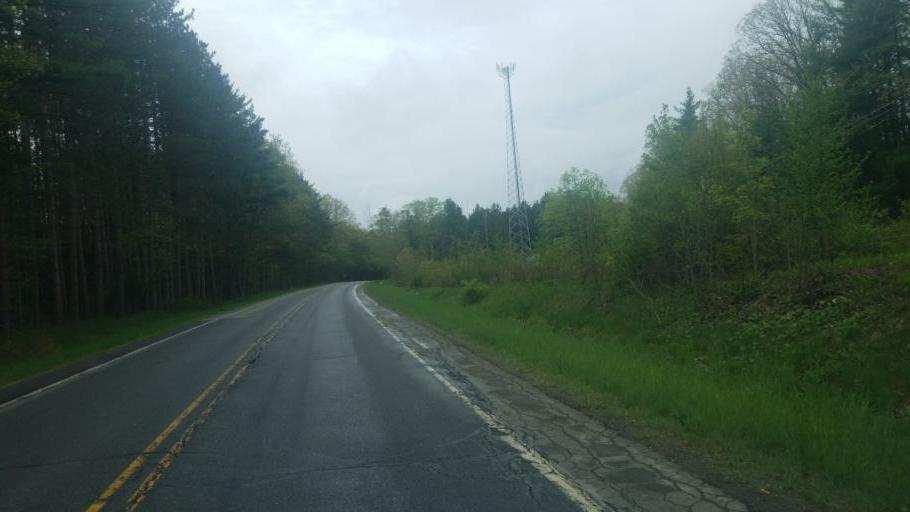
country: US
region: Pennsylvania
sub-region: Forest County
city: Marienville
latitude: 41.4190
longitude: -79.2106
